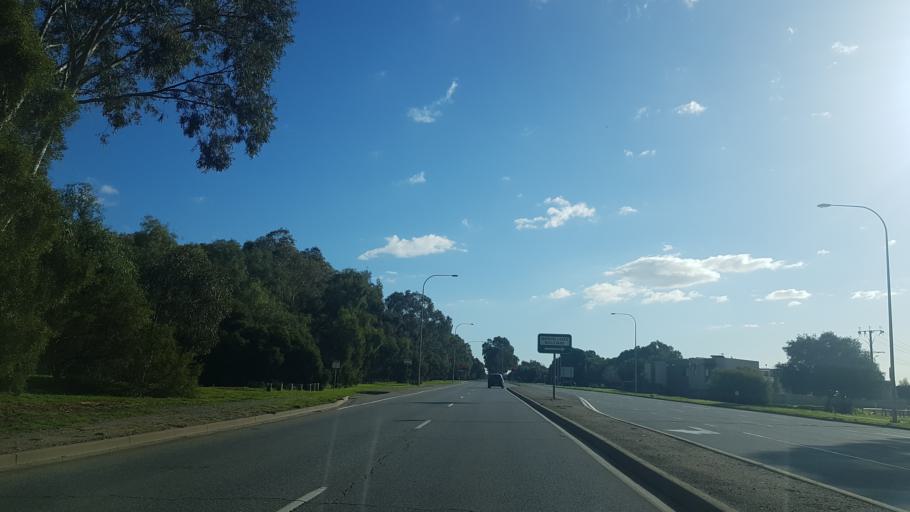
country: AU
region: South Australia
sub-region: Salisbury
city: Ingle Farm
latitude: -34.8247
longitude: 138.6166
